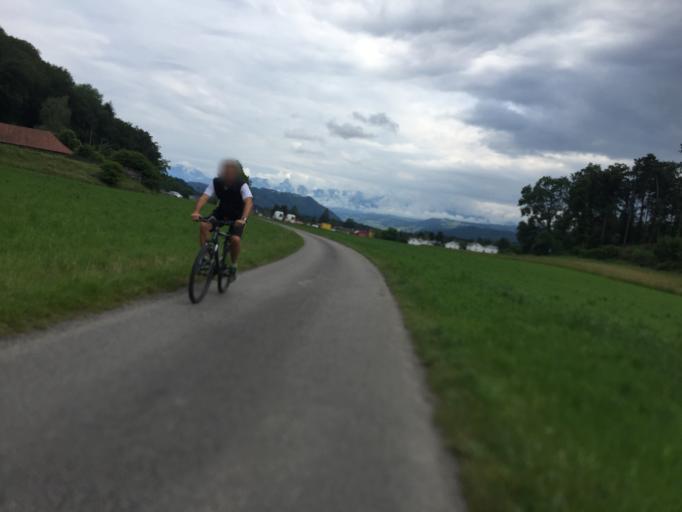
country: CH
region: Bern
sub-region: Bern-Mittelland District
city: Stettlen
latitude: 46.9421
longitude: 7.5084
